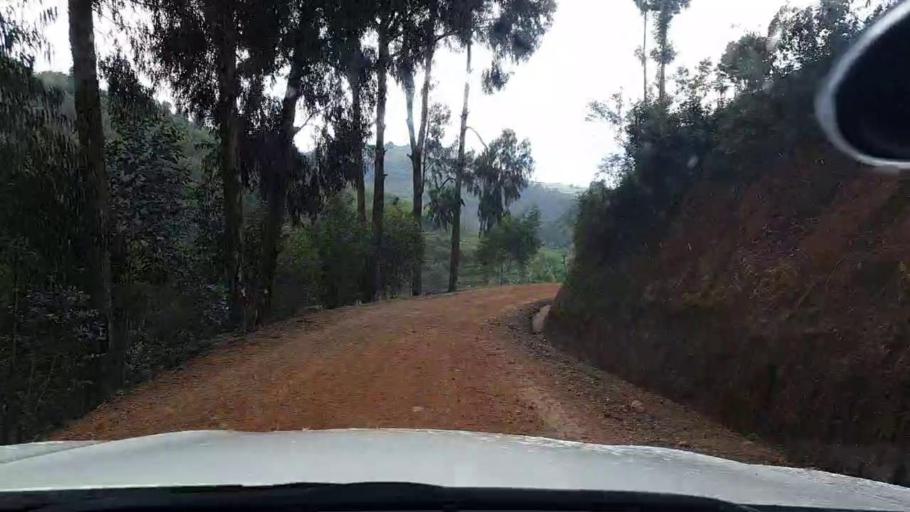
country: RW
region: Western Province
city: Kibuye
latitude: -2.1529
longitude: 29.4288
